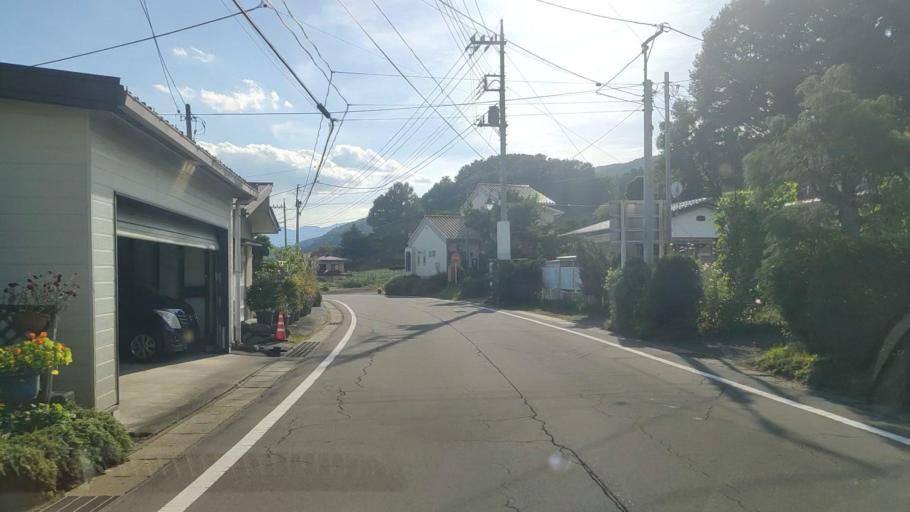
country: JP
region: Nagano
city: Komoro
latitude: 36.5423
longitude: 138.5560
